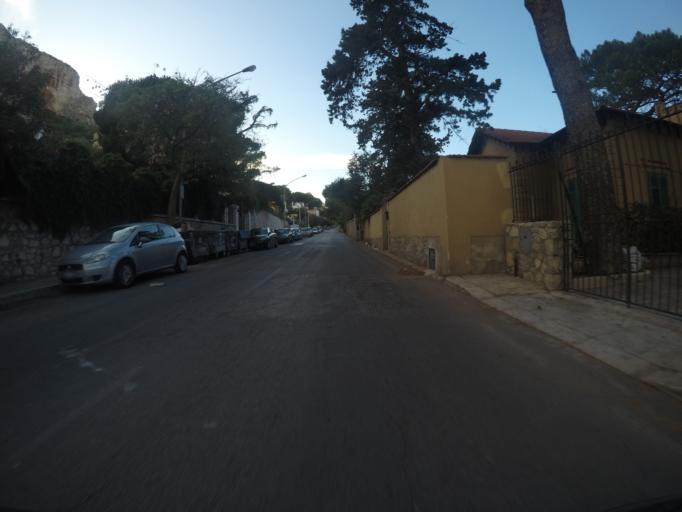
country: IT
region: Sicily
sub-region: Palermo
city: Isola delle Femmine
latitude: 38.1988
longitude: 13.2706
